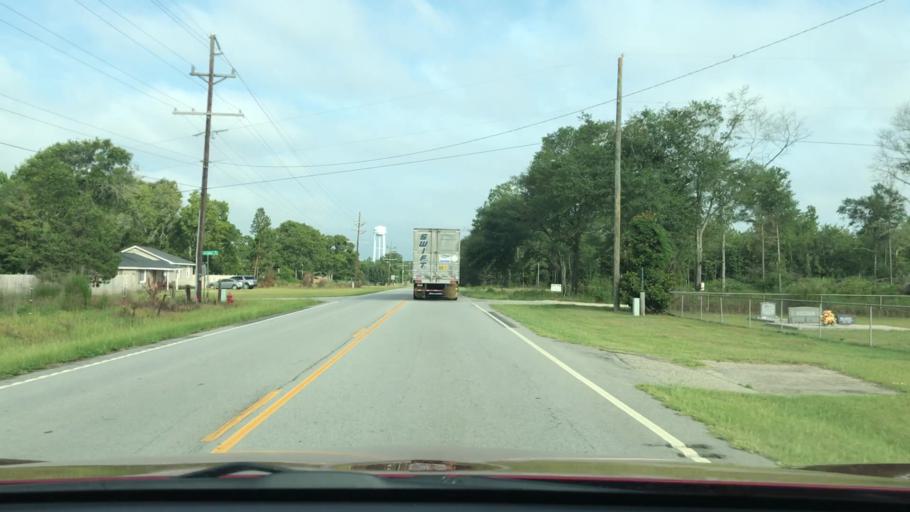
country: US
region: South Carolina
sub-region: Barnwell County
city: Williston
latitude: 33.6364
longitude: -81.3231
